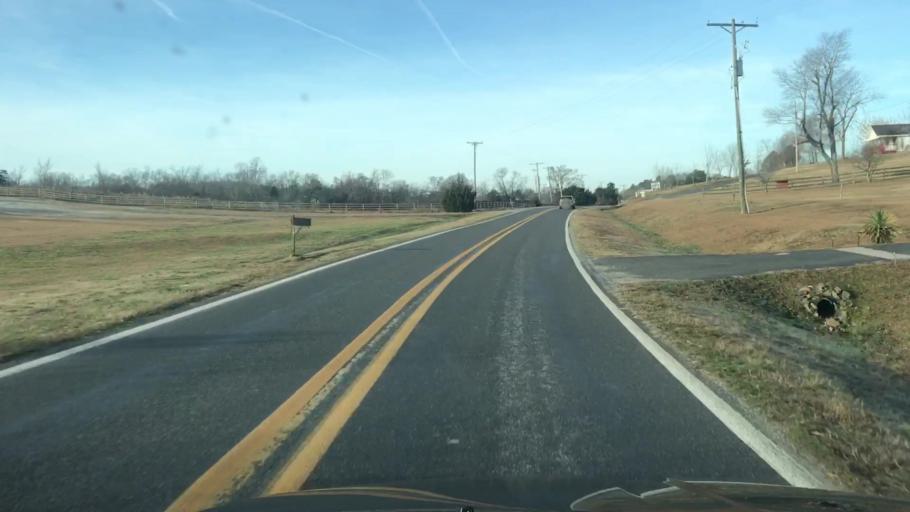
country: US
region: Arkansas
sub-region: Garland County
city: Rockwell
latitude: 34.4723
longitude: -93.2417
